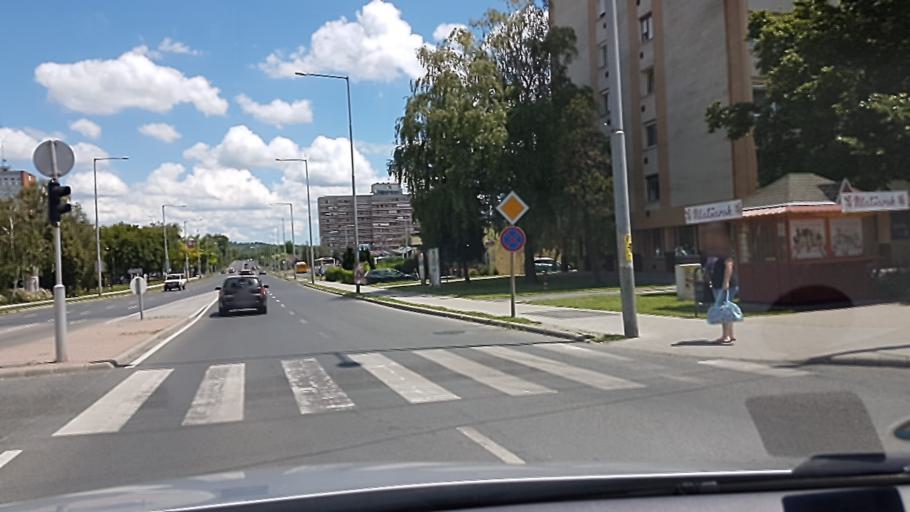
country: HU
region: Zala
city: Zalaegerszeg
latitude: 46.8453
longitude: 16.8473
